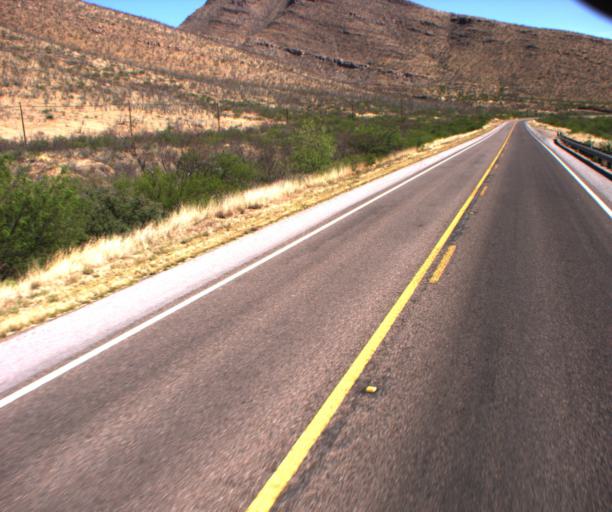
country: US
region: Arizona
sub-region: Cochise County
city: Bisbee
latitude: 31.4370
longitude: -109.8394
